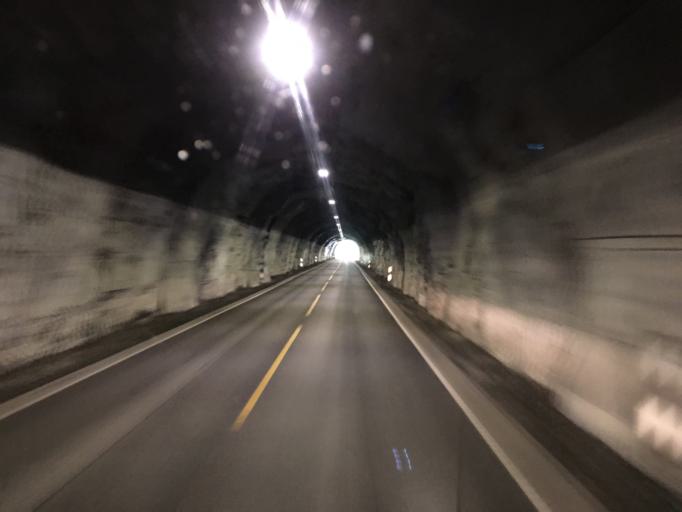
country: NO
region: More og Romsdal
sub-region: Tingvoll
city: Tingvoll
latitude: 62.9712
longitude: 8.0751
